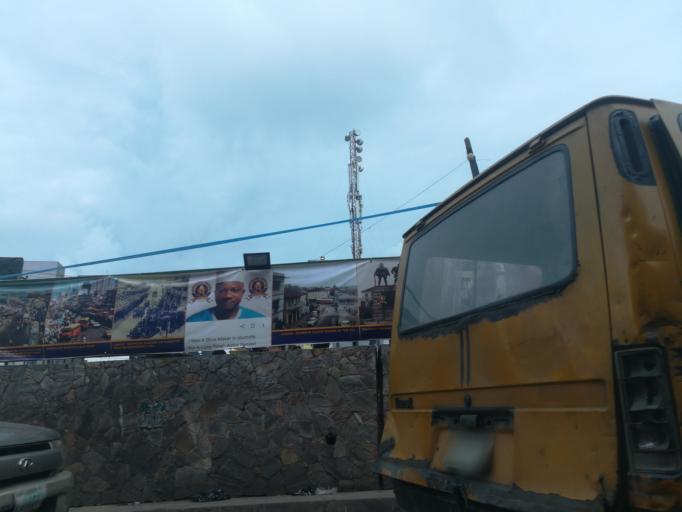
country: NG
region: Lagos
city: Lagos
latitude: 6.4614
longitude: 3.3870
